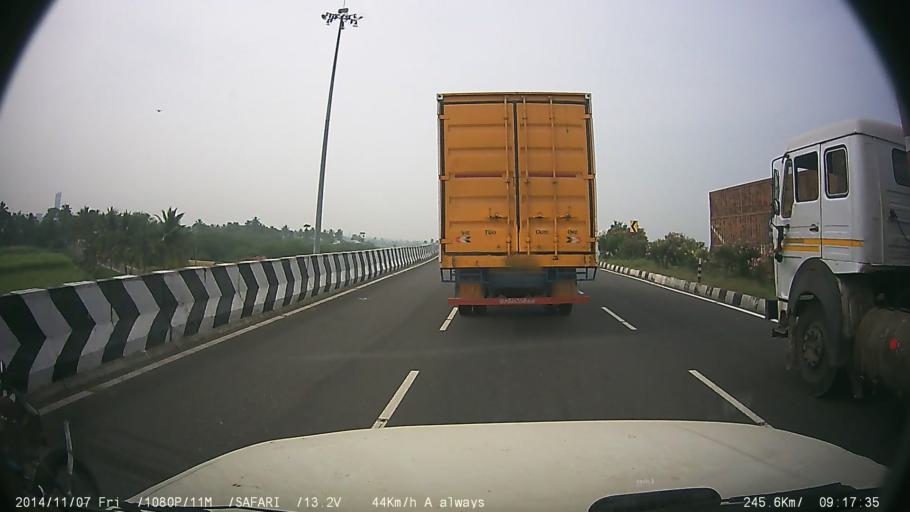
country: IN
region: Tamil Nadu
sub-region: Namakkal
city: Tiruchengode
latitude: 11.4682
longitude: 77.8237
